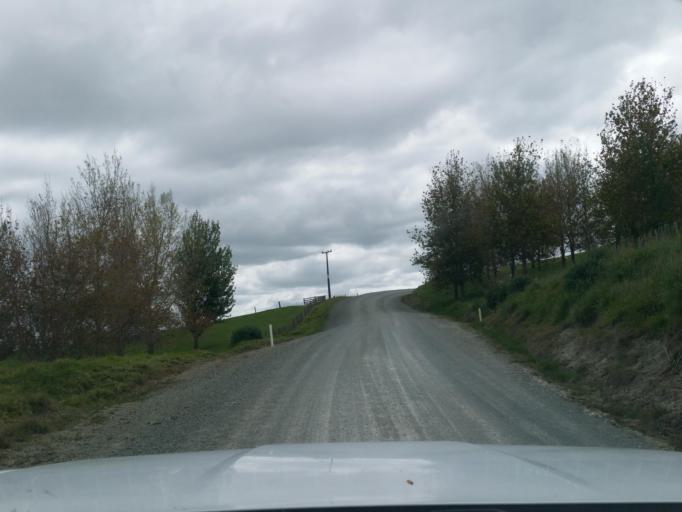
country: NZ
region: Auckland
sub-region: Auckland
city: Wellsford
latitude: -36.2806
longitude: 174.3642
